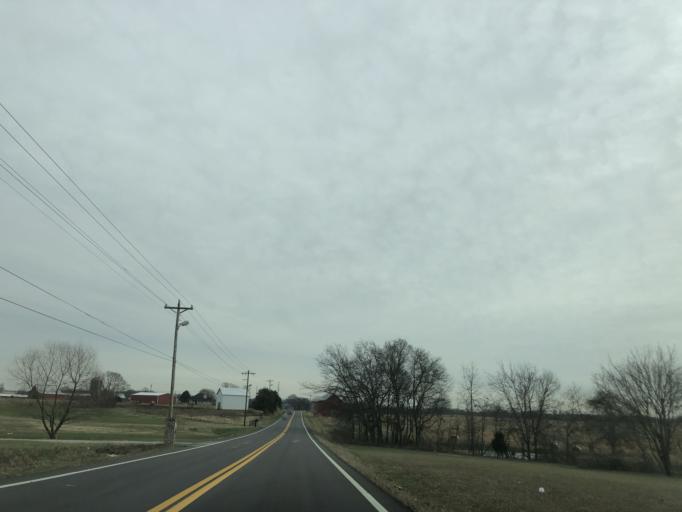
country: US
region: Tennessee
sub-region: Sumner County
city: White House
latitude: 36.4718
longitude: -86.7017
